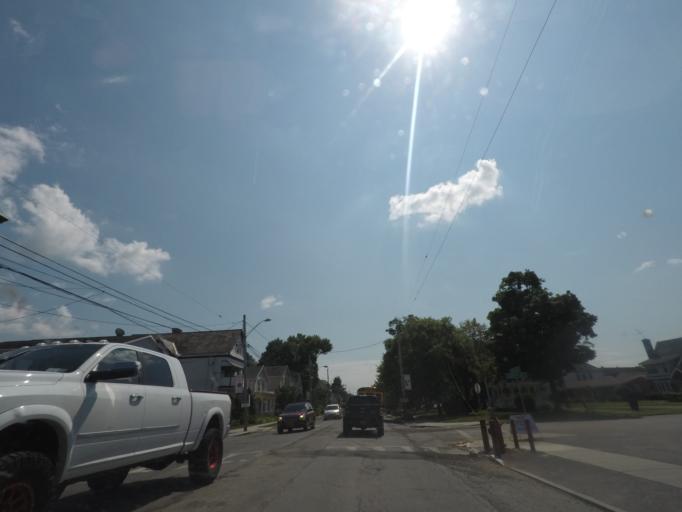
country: US
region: New York
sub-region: Albany County
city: Watervliet
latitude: 42.7132
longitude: -73.7073
